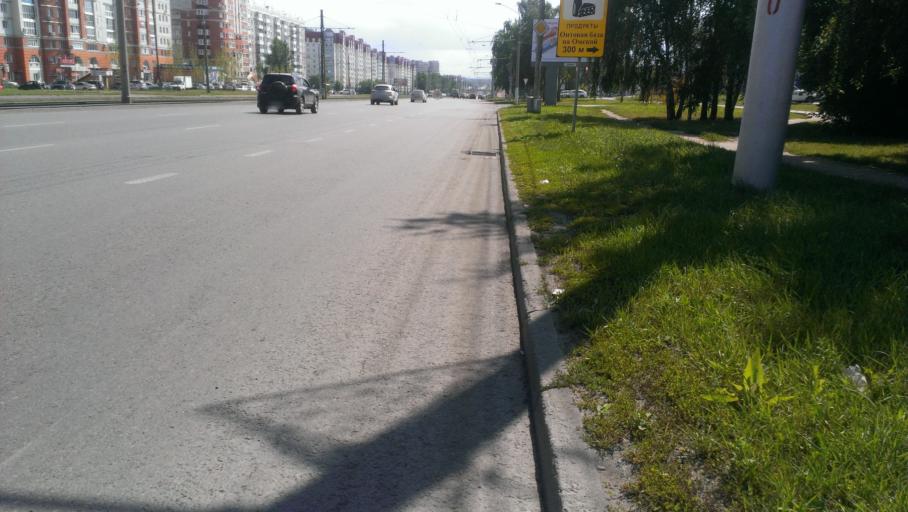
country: RU
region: Altai Krai
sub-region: Gorod Barnaulskiy
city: Barnaul
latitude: 53.3539
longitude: 83.6978
